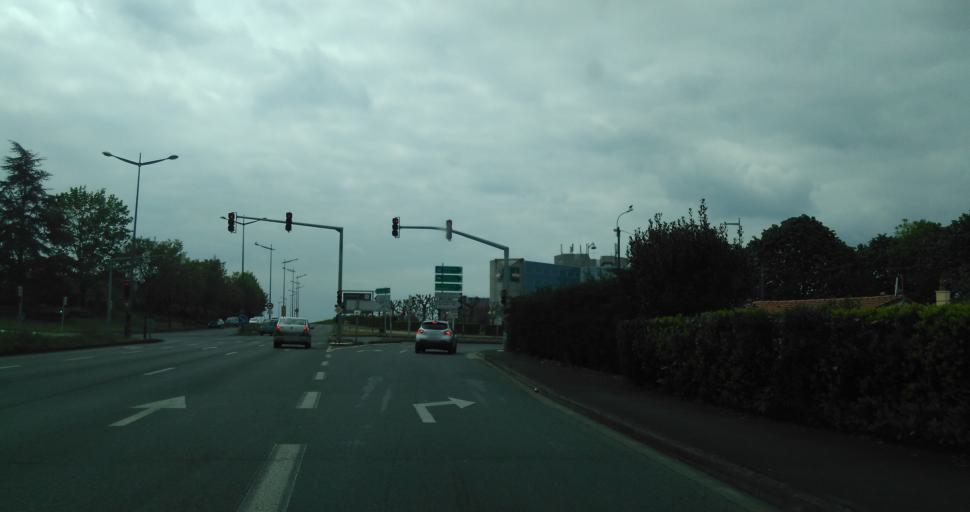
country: FR
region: Poitou-Charentes
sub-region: Departement des Deux-Sevres
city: Niort
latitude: 46.3321
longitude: -0.4825
